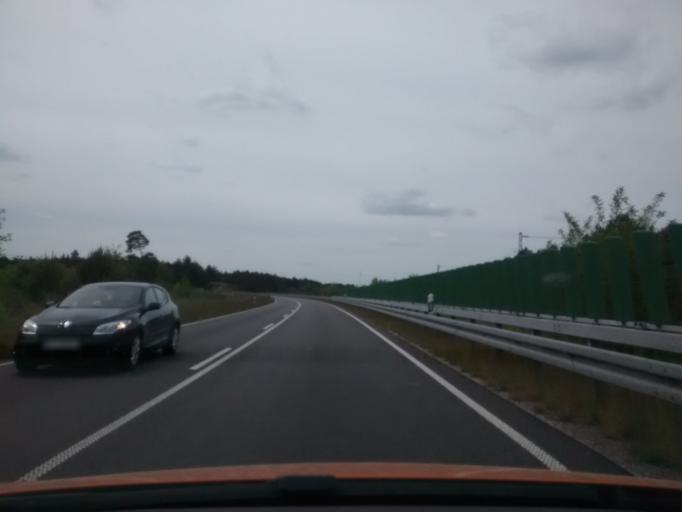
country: DE
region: Brandenburg
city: Luckenwalde
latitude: 52.0606
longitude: 13.1099
